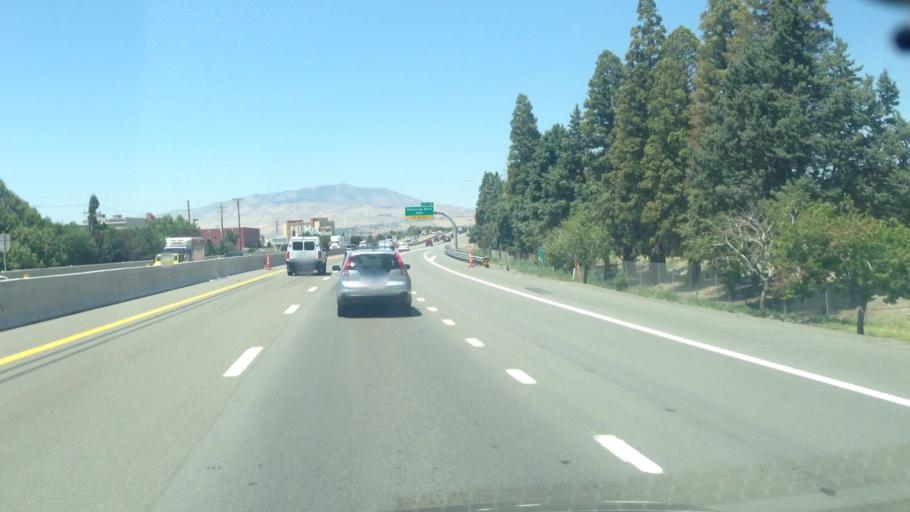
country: US
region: Nevada
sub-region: Washoe County
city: Sparks
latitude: 39.5302
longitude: -119.7310
